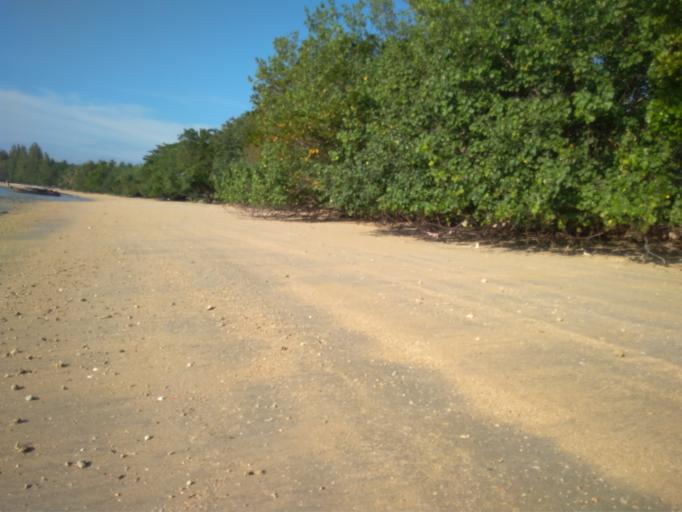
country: TH
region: Phangnga
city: Ko Yao
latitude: 8.1017
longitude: 98.6218
